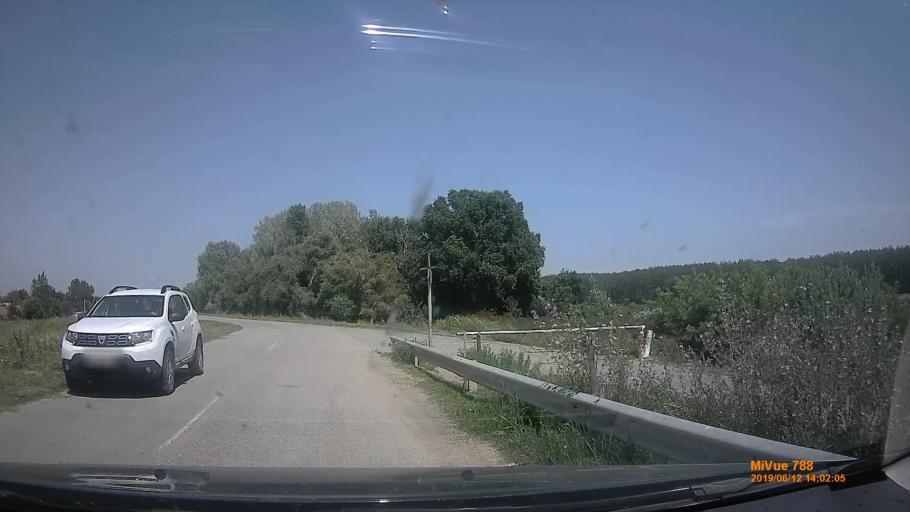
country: HU
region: Csongrad
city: Szeged
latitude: 46.2567
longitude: 20.2022
